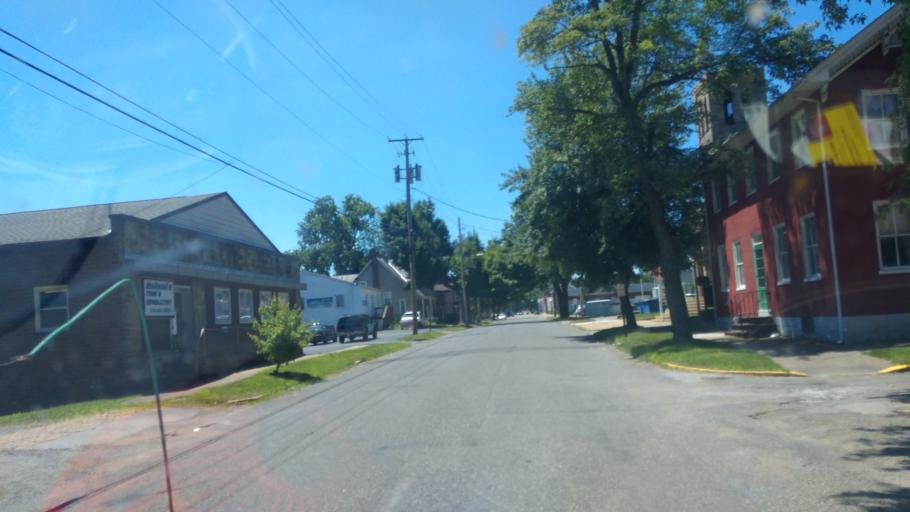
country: US
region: Ohio
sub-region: Columbiana County
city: Lisbon
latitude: 40.7710
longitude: -80.7647
